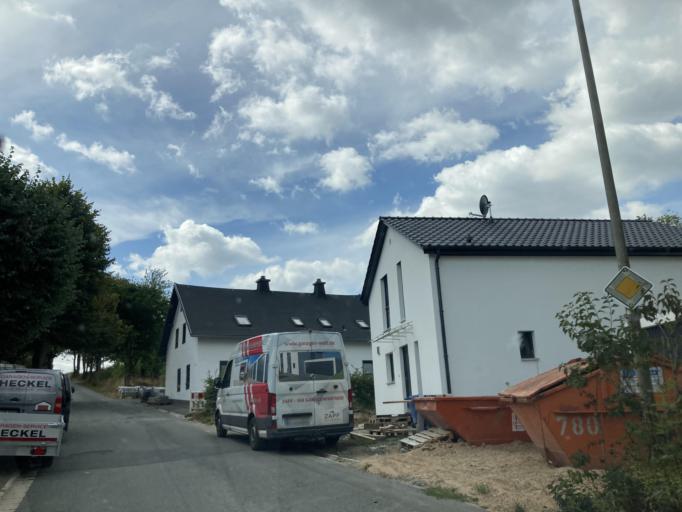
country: DE
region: Bavaria
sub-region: Upper Franconia
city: Grafengehaig
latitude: 50.1823
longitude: 11.5554
